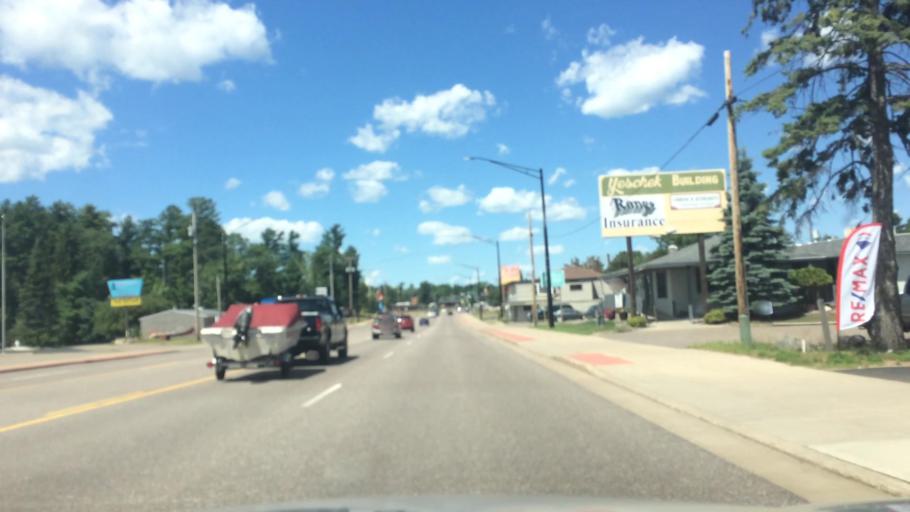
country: US
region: Wisconsin
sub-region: Vilas County
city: Lac du Flambeau
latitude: 45.8812
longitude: -89.7030
